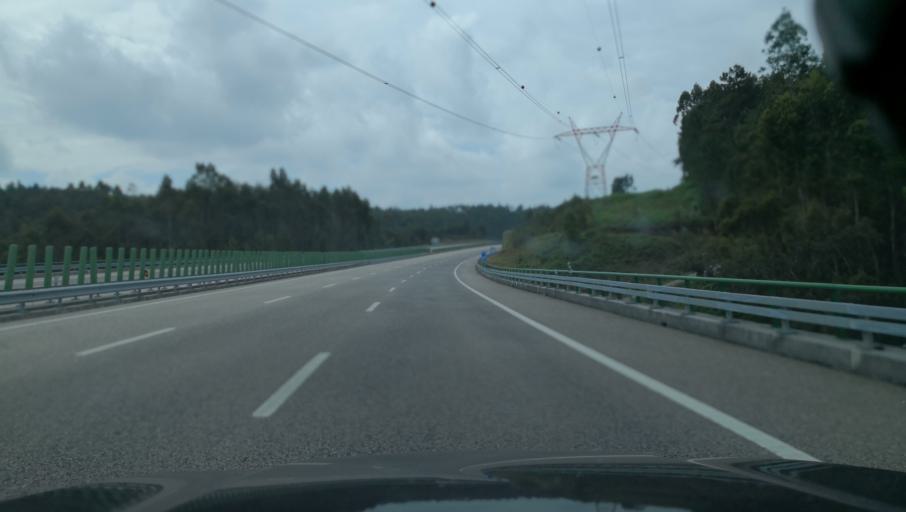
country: PT
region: Leiria
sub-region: Pombal
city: Lourical
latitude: 39.9536
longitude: -8.7728
